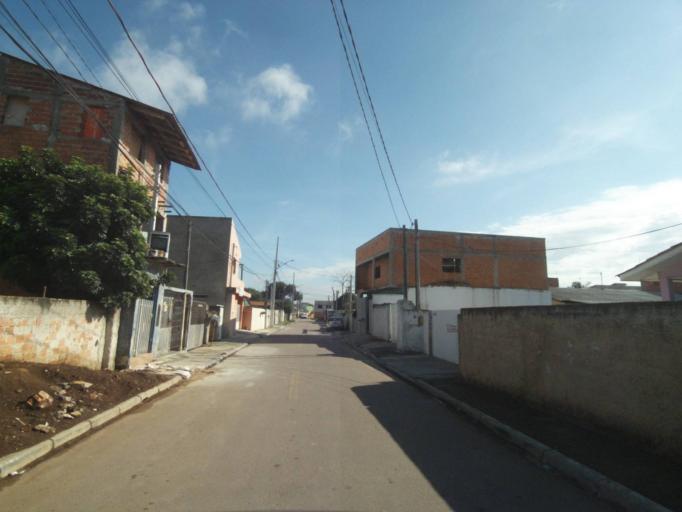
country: BR
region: Parana
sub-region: Pinhais
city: Pinhais
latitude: -25.4715
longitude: -49.1904
